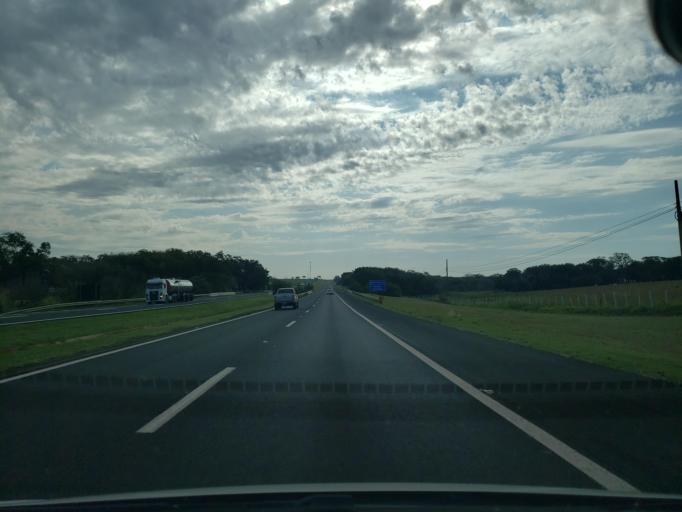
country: BR
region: Sao Paulo
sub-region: Birigui
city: Birigui
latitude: -21.3502
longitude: -50.3130
